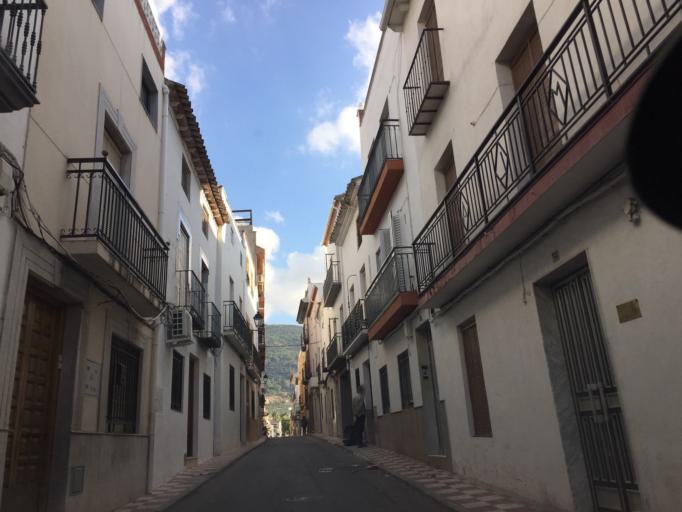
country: ES
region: Andalusia
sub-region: Provincia de Jaen
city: Mancha Real
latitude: 37.7861
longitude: -3.6100
